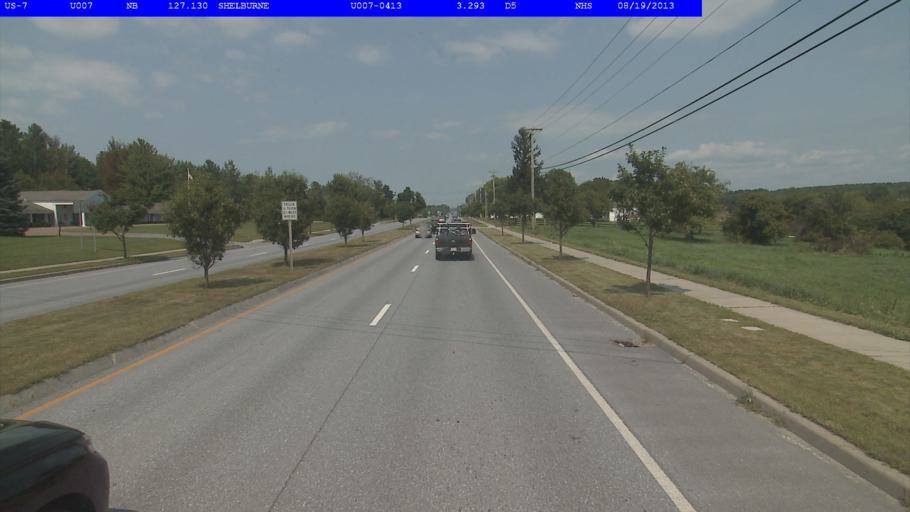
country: US
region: Vermont
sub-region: Chittenden County
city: Burlington
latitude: 44.3979
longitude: -73.2192
